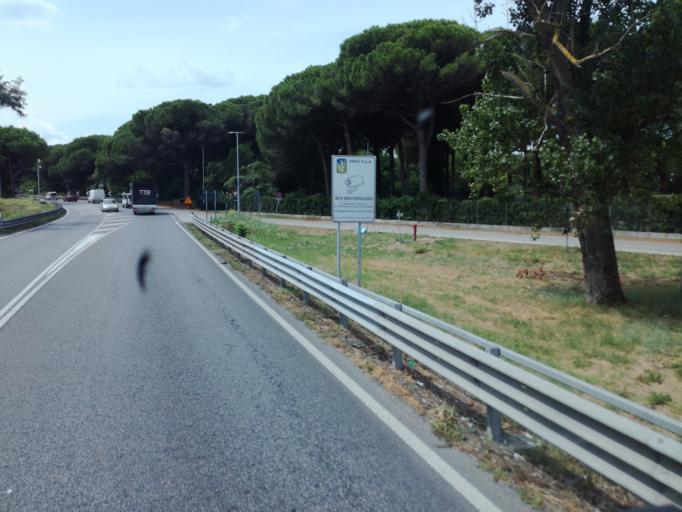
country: IT
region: Emilia-Romagna
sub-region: Provincia di Ferrara
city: Mesola
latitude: 44.9125
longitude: 12.2332
